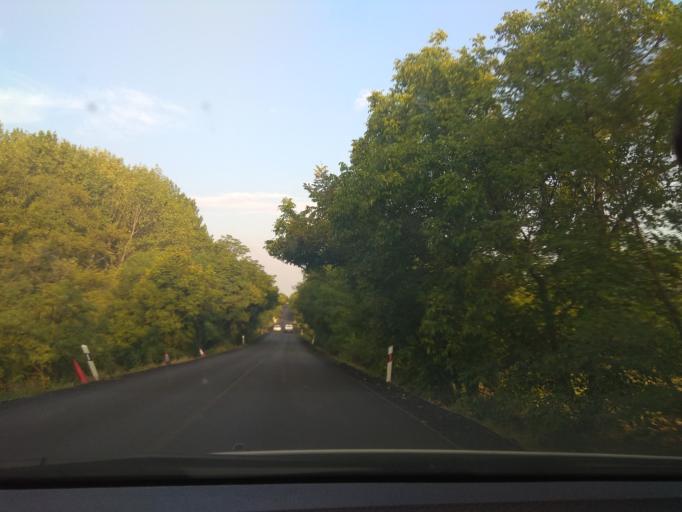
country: HU
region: Heves
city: Szihalom
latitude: 47.8189
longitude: 20.5044
